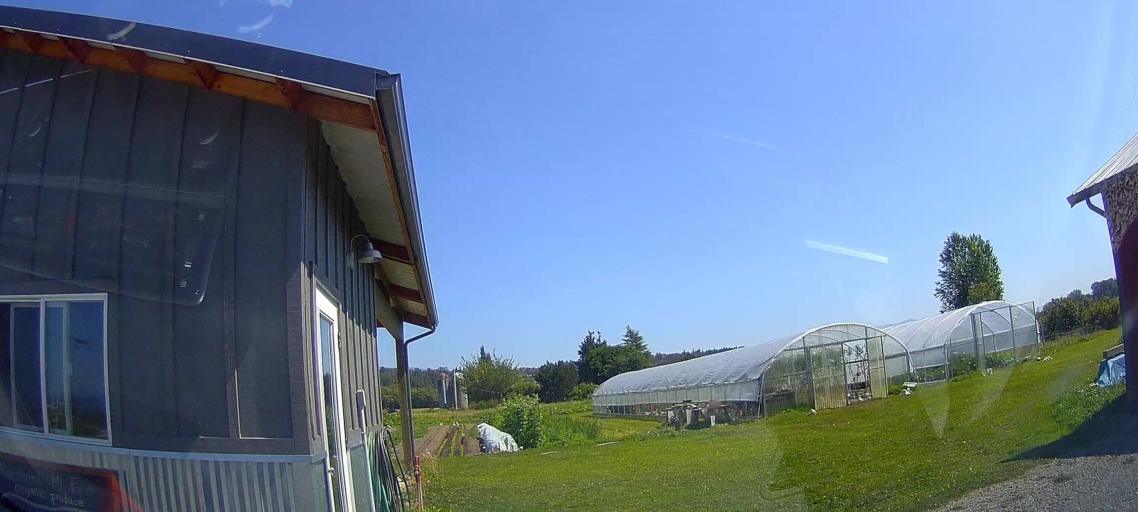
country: US
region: Washington
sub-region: Skagit County
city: Burlington
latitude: 48.5697
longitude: -122.4127
